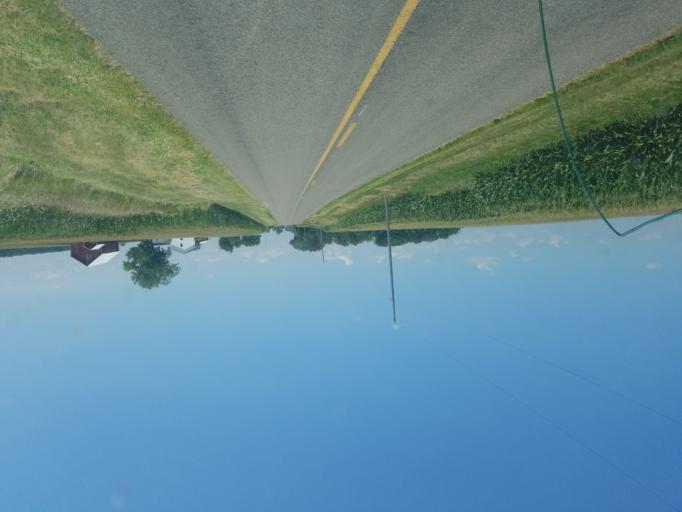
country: US
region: Ohio
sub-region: Shelby County
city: Botkins
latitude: 40.4822
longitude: -84.2162
